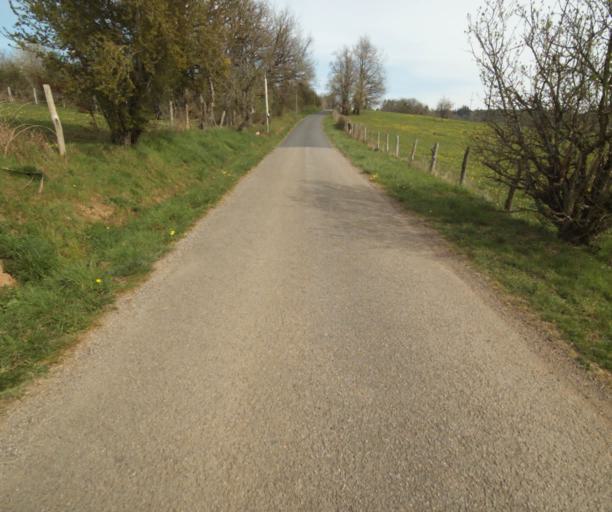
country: FR
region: Limousin
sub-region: Departement de la Correze
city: Correze
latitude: 45.3771
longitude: 1.8202
